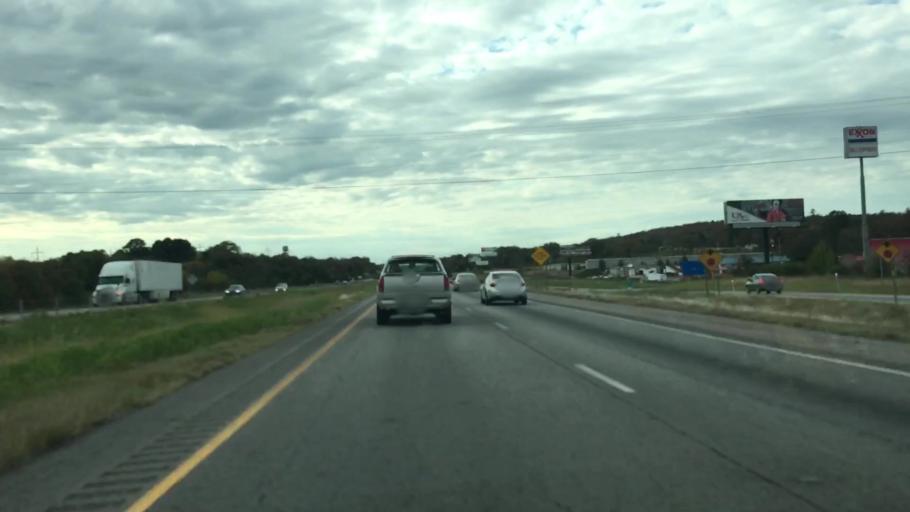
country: US
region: Arkansas
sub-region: Conway County
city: Morrilton
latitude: 35.1631
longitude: -92.6380
